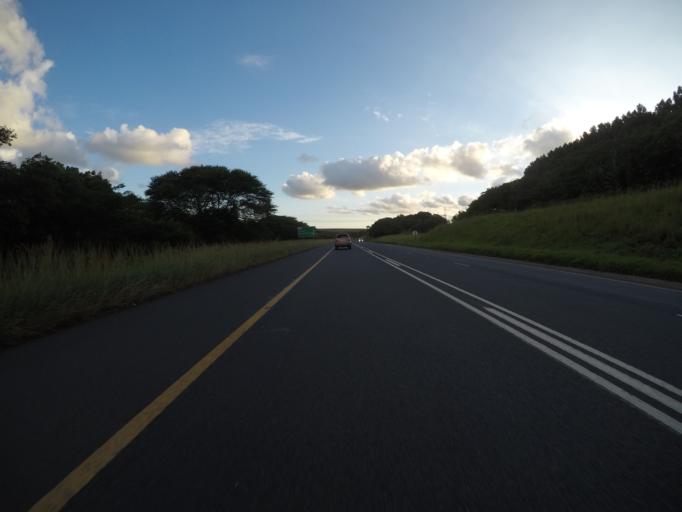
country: ZA
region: KwaZulu-Natal
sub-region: uThungulu District Municipality
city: Richards Bay
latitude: -28.6857
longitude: 32.0398
